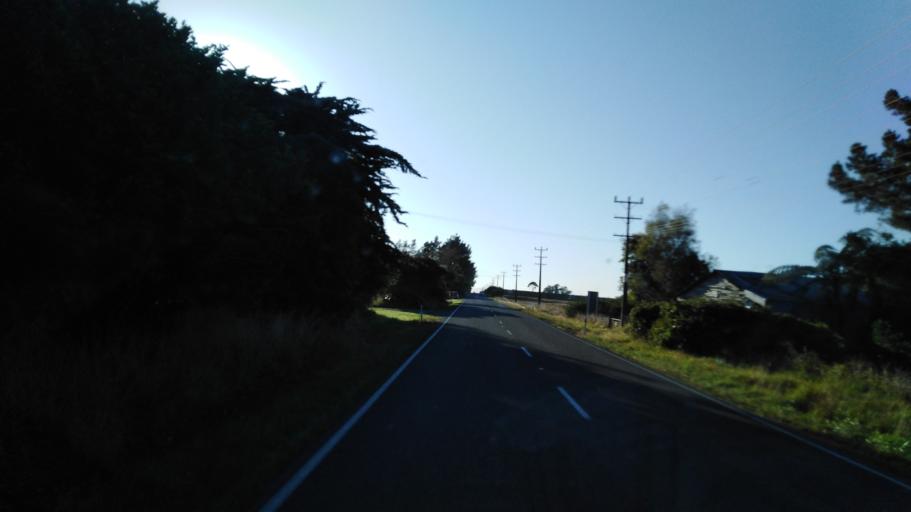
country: NZ
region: Manawatu-Wanganui
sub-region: Rangitikei District
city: Bulls
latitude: -40.0676
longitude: 175.4041
